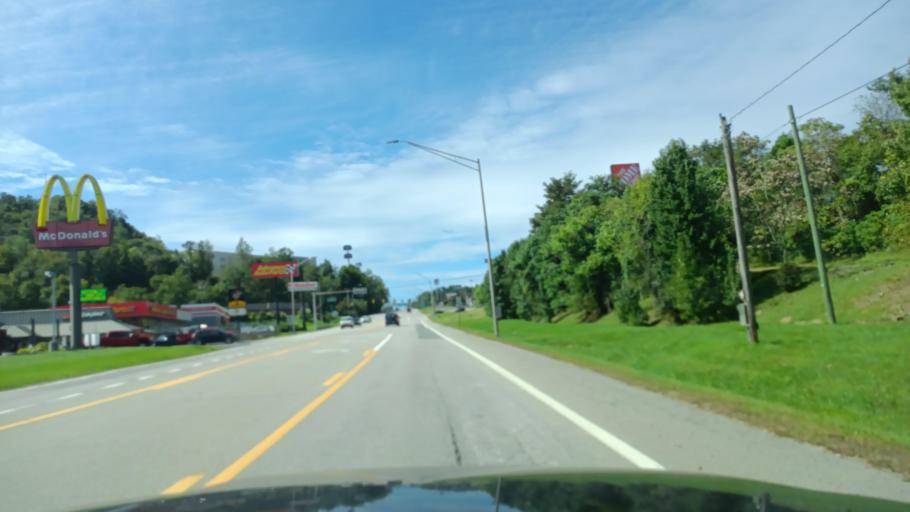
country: US
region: West Virginia
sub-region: Harrison County
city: Bridgeport
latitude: 39.2816
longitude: -80.2716
